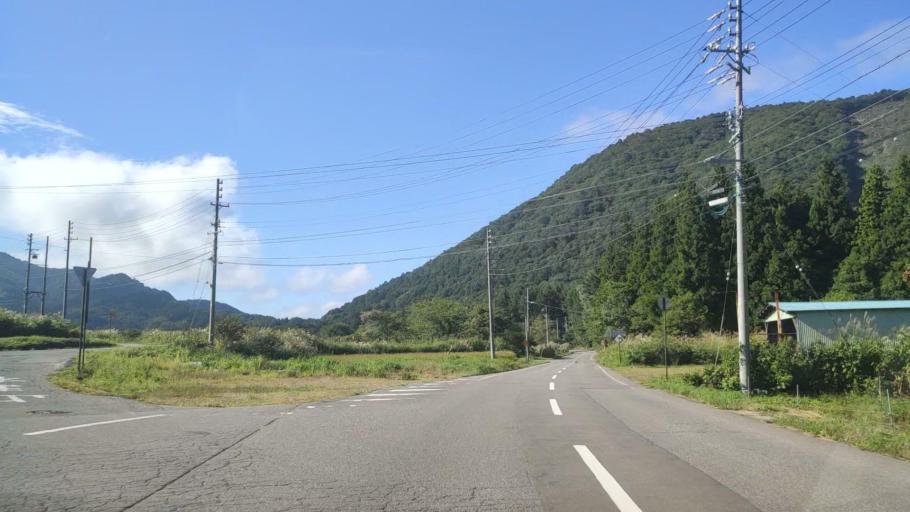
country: JP
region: Nagano
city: Nakano
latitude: 36.7921
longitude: 138.4338
